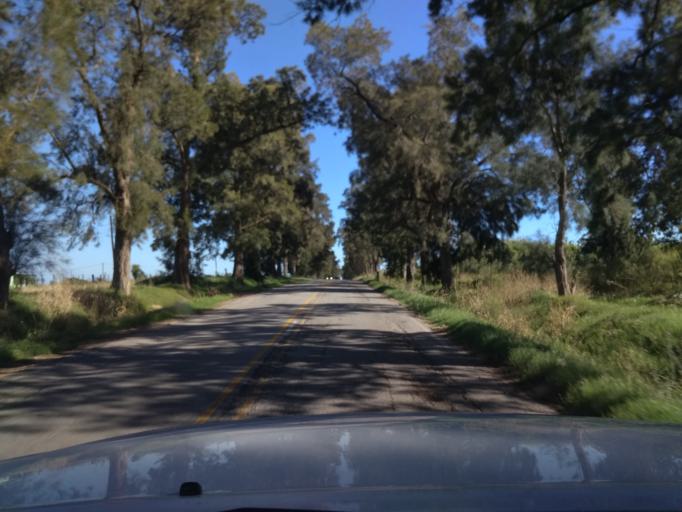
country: UY
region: Canelones
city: San Ramon
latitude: -34.3681
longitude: -55.9595
